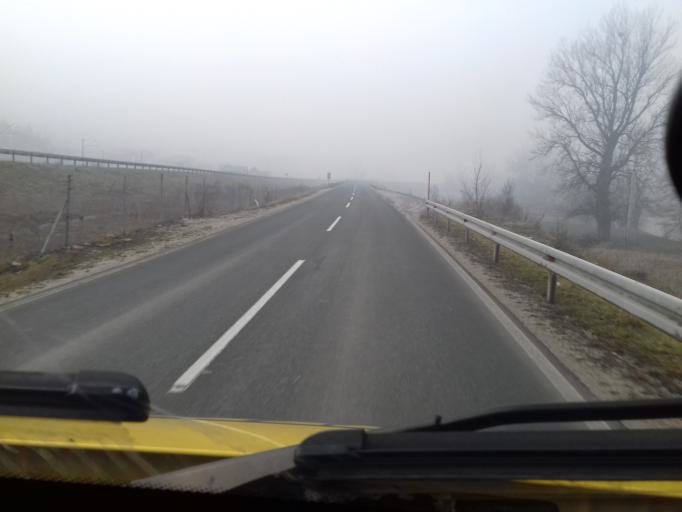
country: BA
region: Federation of Bosnia and Herzegovina
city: Kakanj
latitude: 44.1327
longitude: 18.0719
